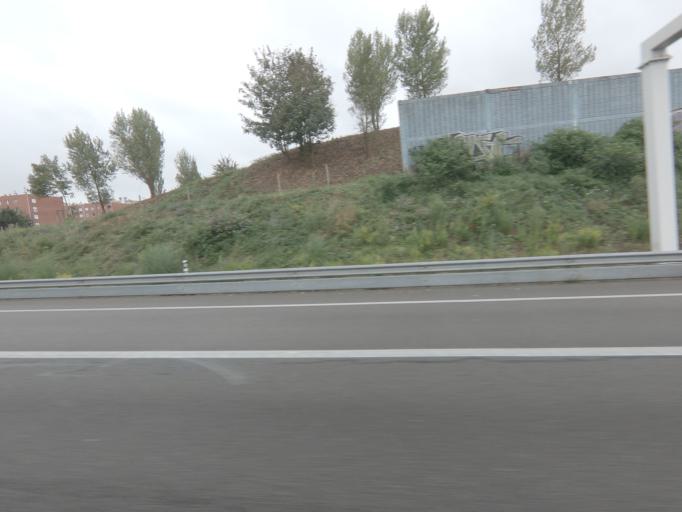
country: PT
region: Porto
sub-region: Matosinhos
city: Sao Mamede de Infesta
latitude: 41.2002
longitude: -8.6073
